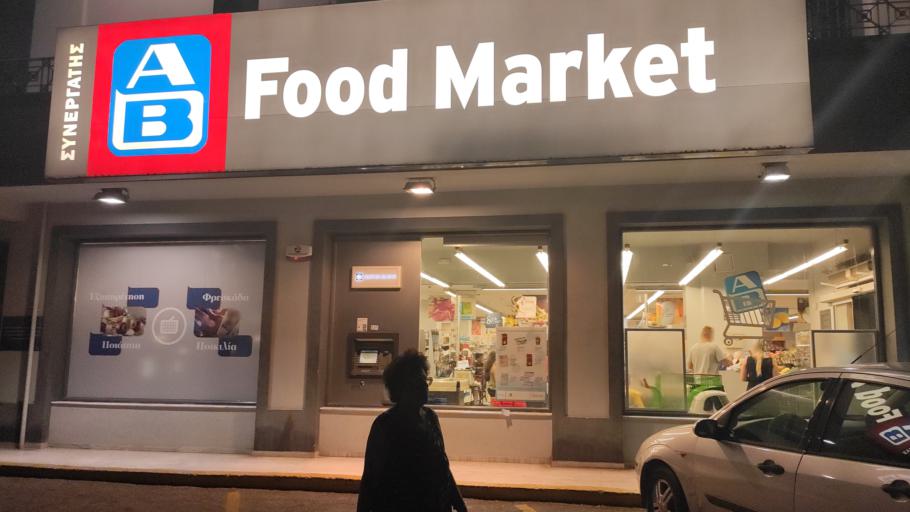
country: GR
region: South Aegean
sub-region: Nomos Dodekanisou
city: Kos
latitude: 36.9024
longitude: 27.2822
